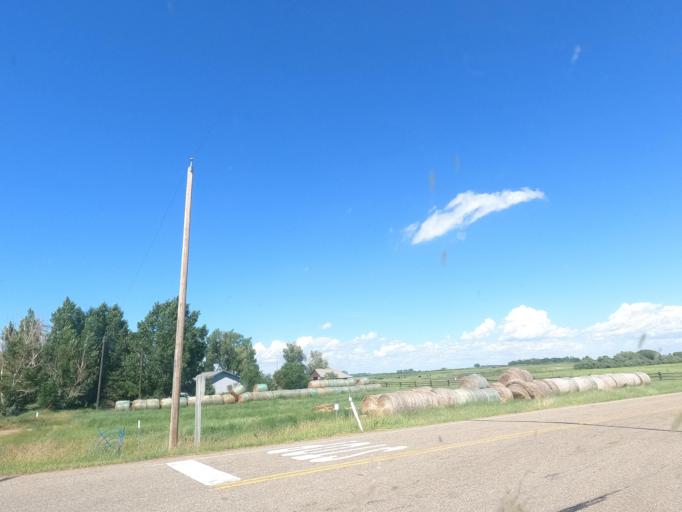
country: CA
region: Alberta
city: Brooks
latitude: 50.7178
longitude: -111.6661
